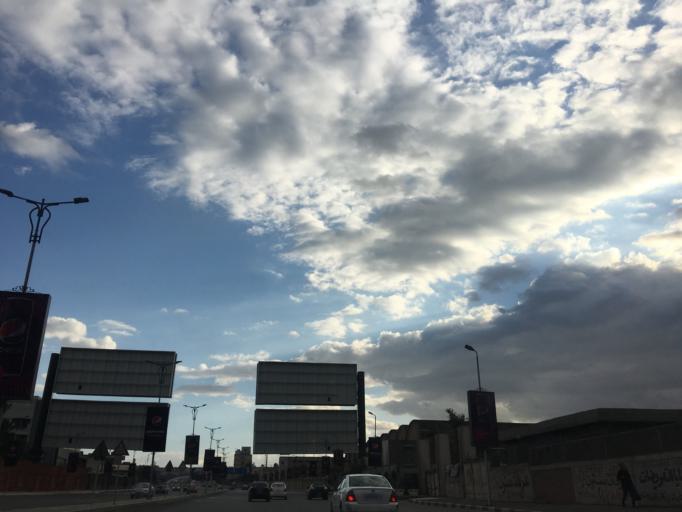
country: EG
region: Muhafazat al Qahirah
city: Cairo
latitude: 30.0493
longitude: 31.3074
